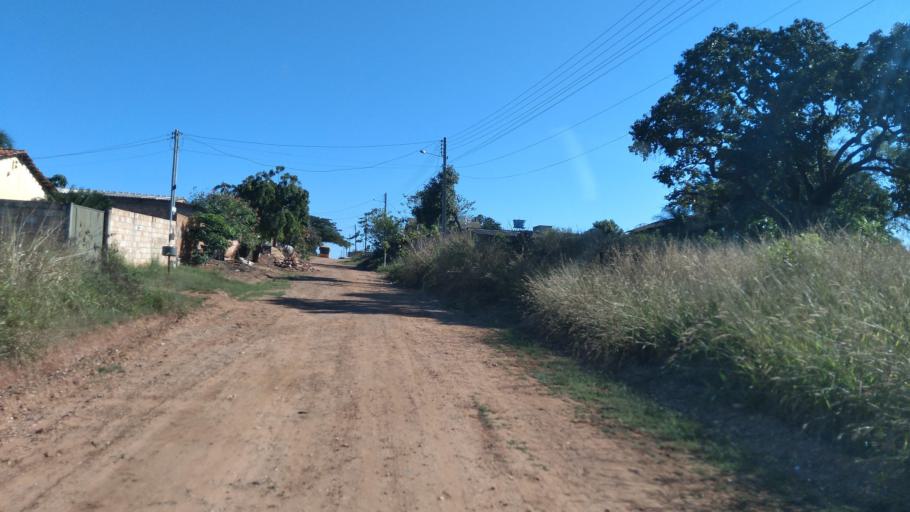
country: BR
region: Goias
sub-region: Mineiros
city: Mineiros
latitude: -17.5943
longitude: -52.5551
